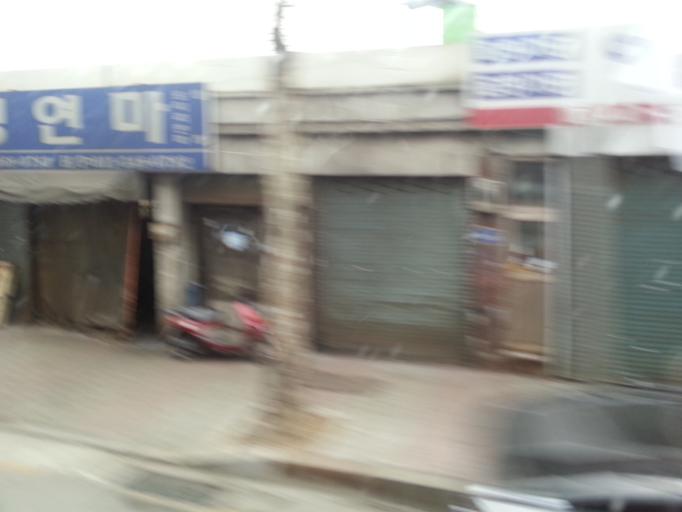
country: KR
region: Gyeonggi-do
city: Anyang-si
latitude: 37.3875
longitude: 126.9342
